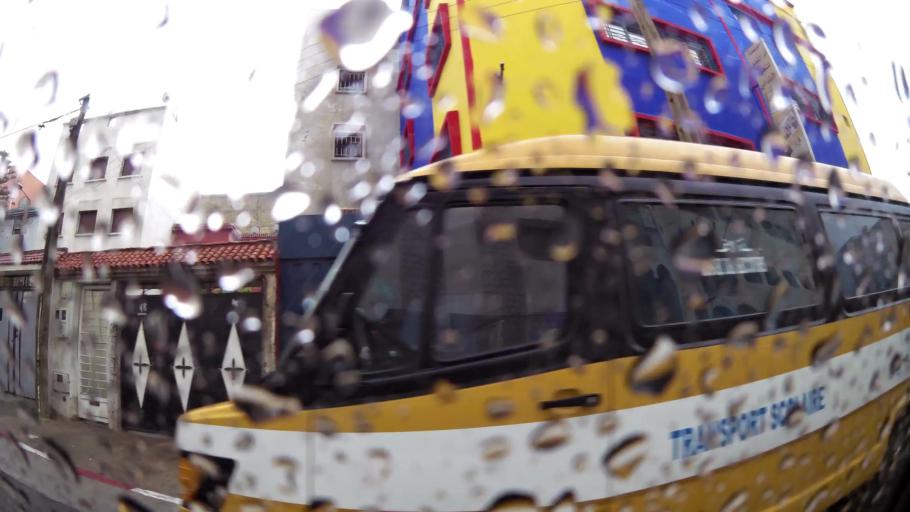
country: MA
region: Grand Casablanca
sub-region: Mediouna
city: Tit Mellil
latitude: 33.6137
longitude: -7.4974
